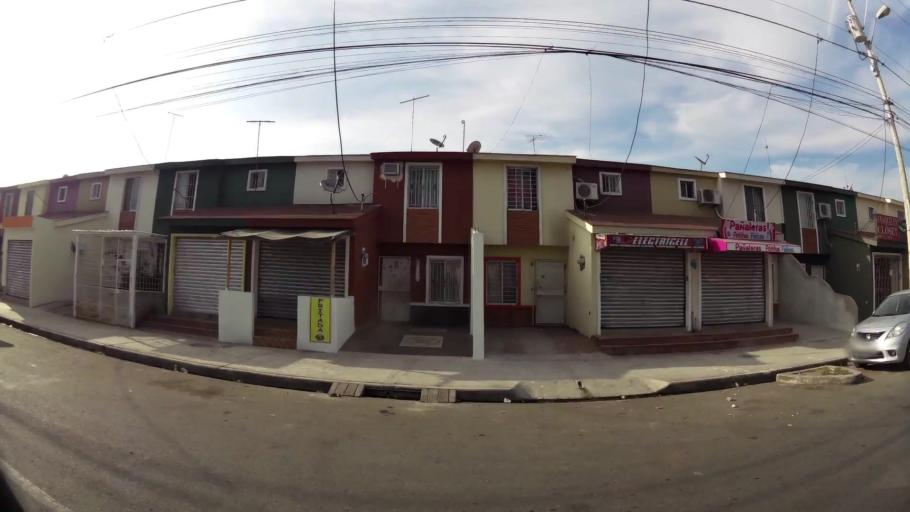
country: EC
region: Guayas
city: Eloy Alfaro
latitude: -2.0668
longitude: -79.8969
